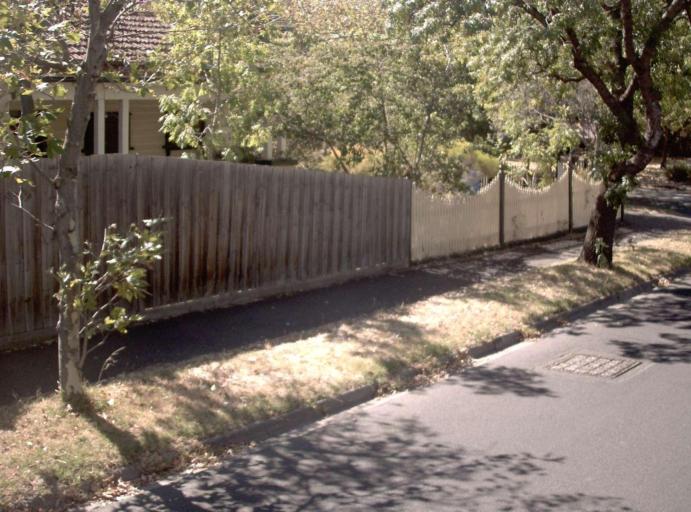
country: AU
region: Victoria
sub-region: Bayside
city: Hampton
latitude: -37.9265
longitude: 145.0045
